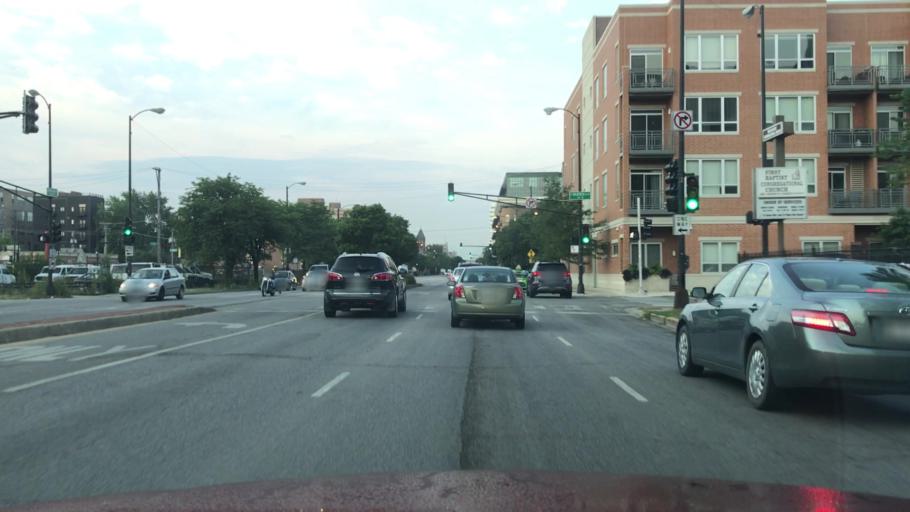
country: US
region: Illinois
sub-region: Cook County
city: Chicago
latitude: 41.8828
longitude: -87.6669
